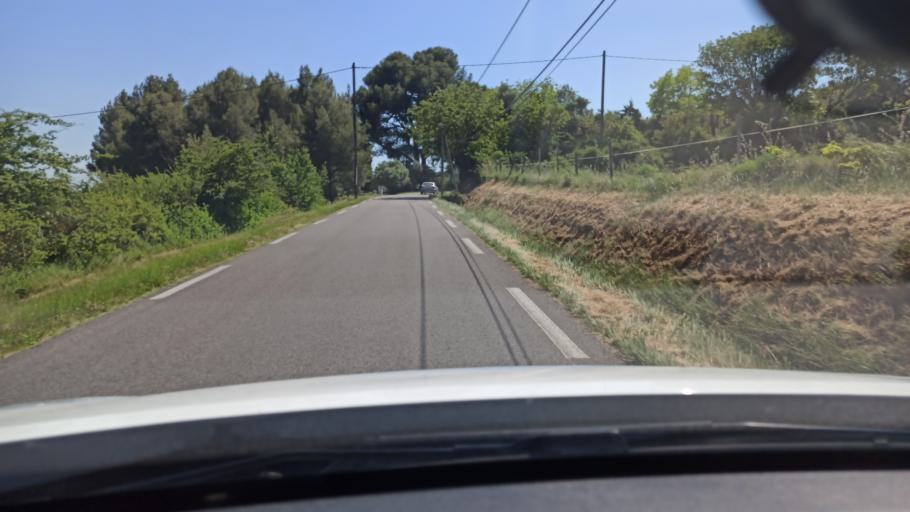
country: FR
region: Provence-Alpes-Cote d'Azur
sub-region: Departement des Bouches-du-Rhone
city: Noves
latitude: 43.8710
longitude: 4.8858
